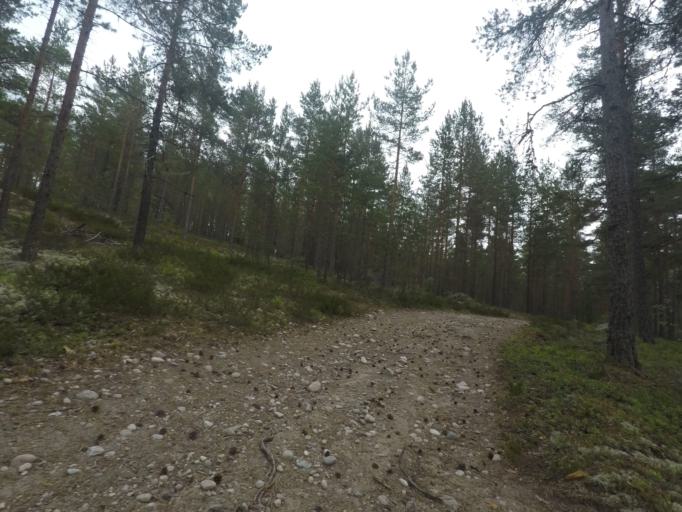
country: SE
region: Vaestmanland
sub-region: Kungsors Kommun
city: Kungsoer
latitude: 59.3703
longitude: 16.1071
